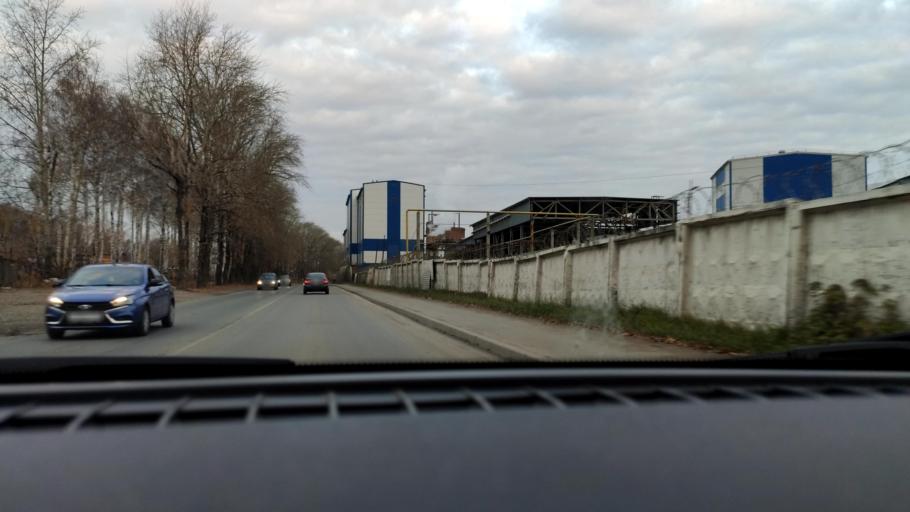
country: RU
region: Perm
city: Perm
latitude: 57.9574
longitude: 56.2126
